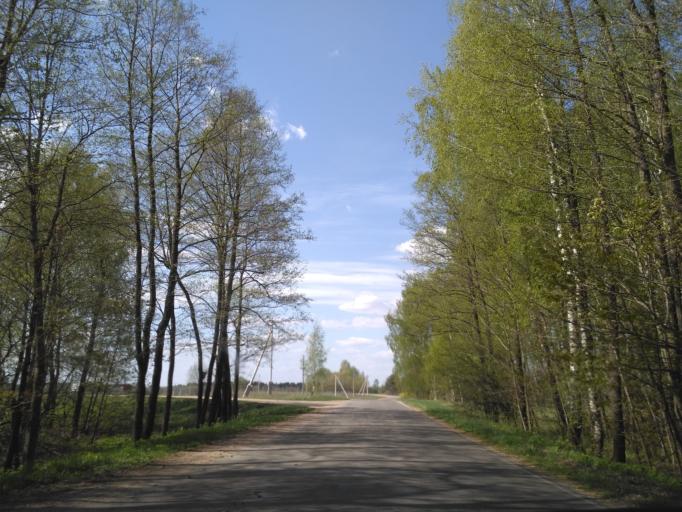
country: BY
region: Minsk
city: Narach
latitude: 54.9644
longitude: 26.6417
